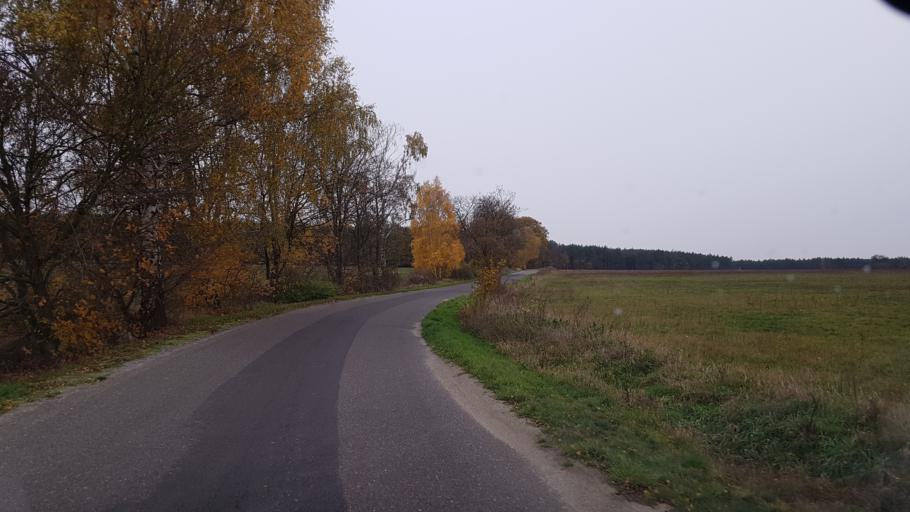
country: DE
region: Brandenburg
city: Crinitz
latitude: 51.7319
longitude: 13.7633
